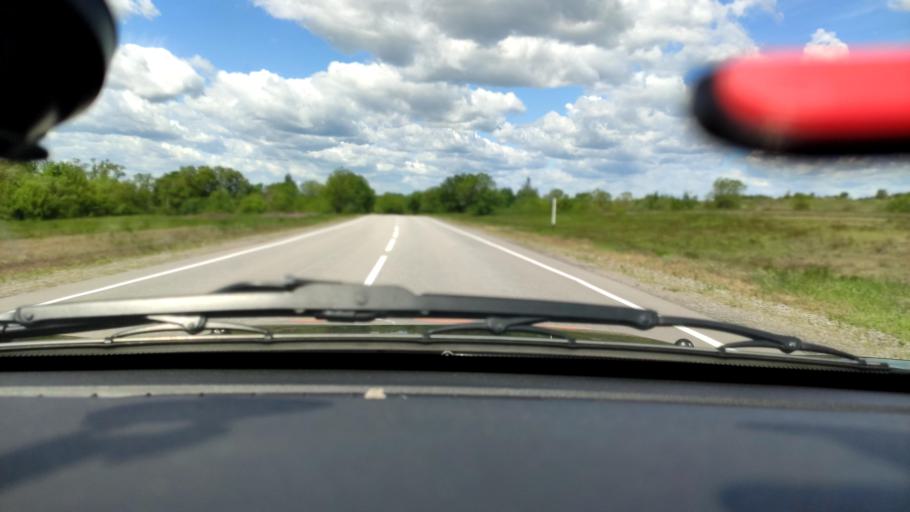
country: RU
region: Voronezj
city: Ostrogozhsk
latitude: 51.0542
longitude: 38.9297
